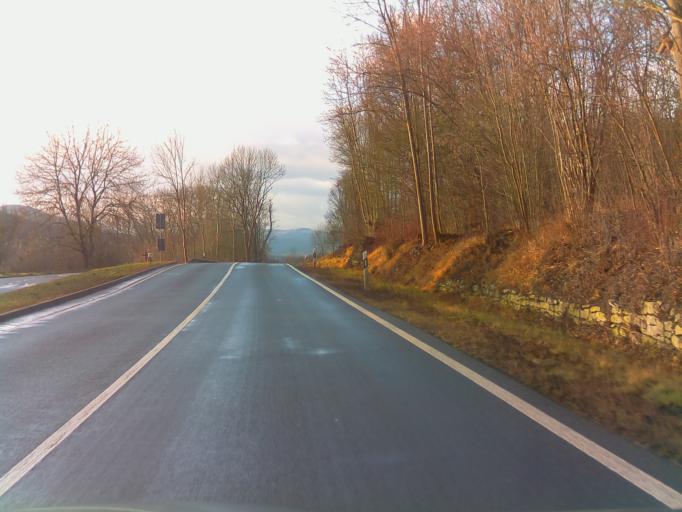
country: DE
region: Thuringia
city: Arnstadt
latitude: 50.8157
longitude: 10.9374
